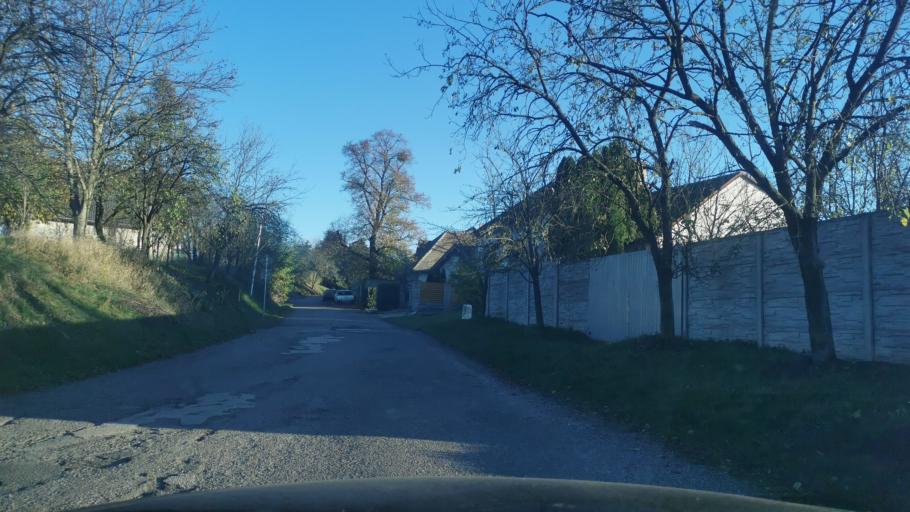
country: SK
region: Trnavsky
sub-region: Okres Skalica
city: Skalica
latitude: 48.7743
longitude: 17.2803
